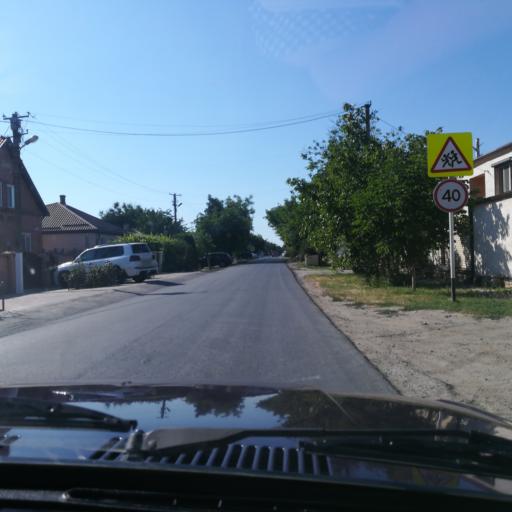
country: RU
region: Krasnodarskiy
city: Vityazevo
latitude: 45.0024
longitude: 37.2877
